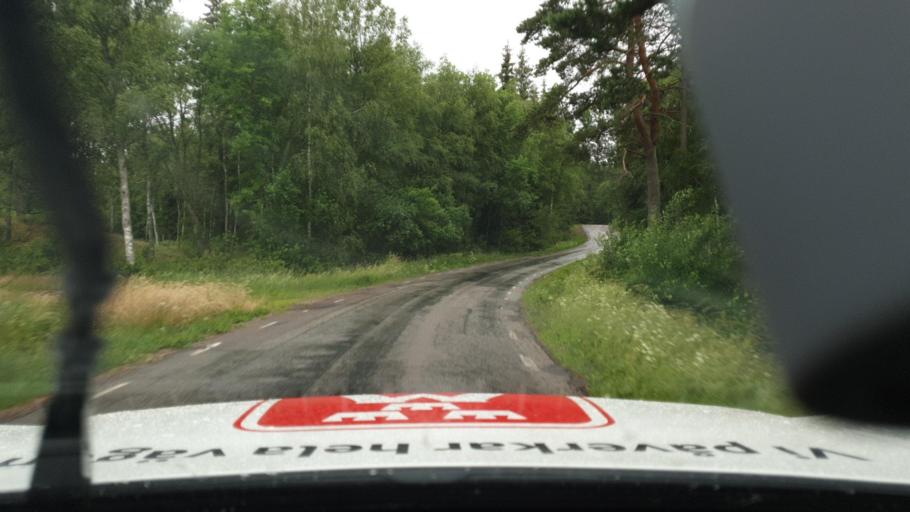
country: SE
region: Joenkoeping
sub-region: Mullsjo Kommun
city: Mullsjoe
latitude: 57.9563
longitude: 13.6455
